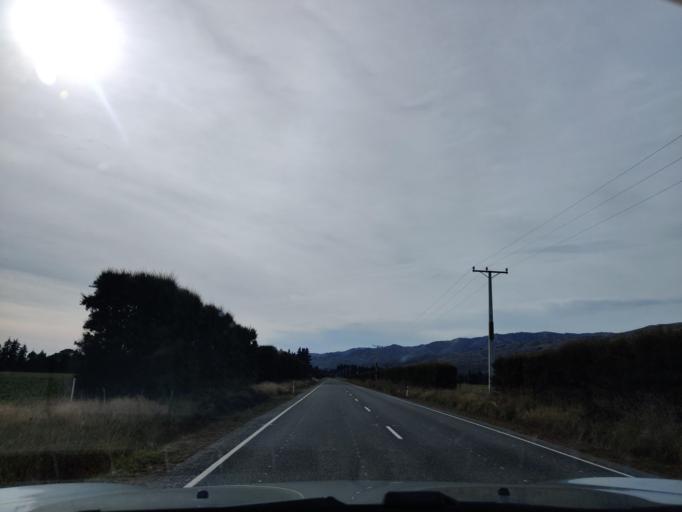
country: NZ
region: Tasman
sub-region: Tasman District
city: Brightwater
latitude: -41.6532
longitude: 173.2632
